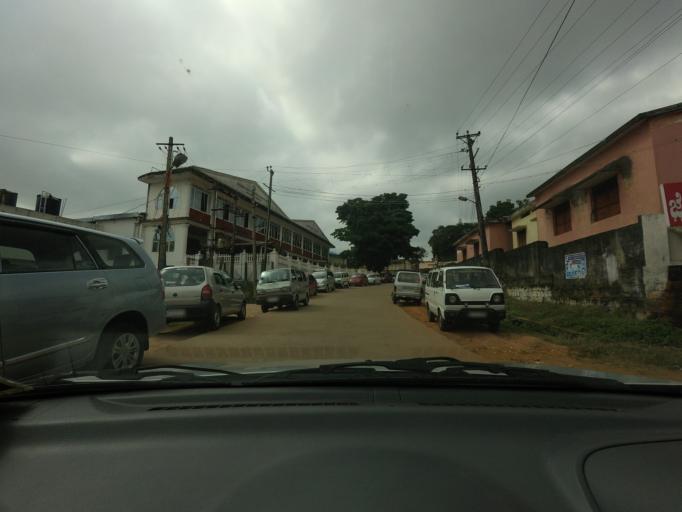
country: IN
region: Karnataka
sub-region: Hassan
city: Sakleshpur
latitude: 12.9451
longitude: 75.7868
